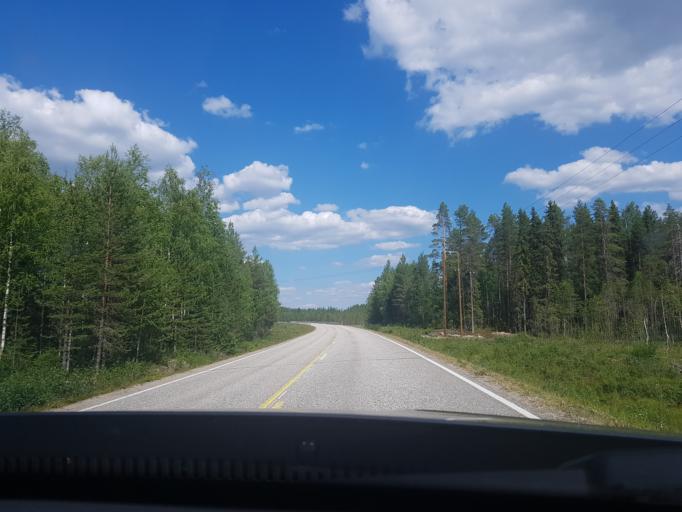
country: FI
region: Kainuu
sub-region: Kehys-Kainuu
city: Kuhmo
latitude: 64.2206
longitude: 29.7968
